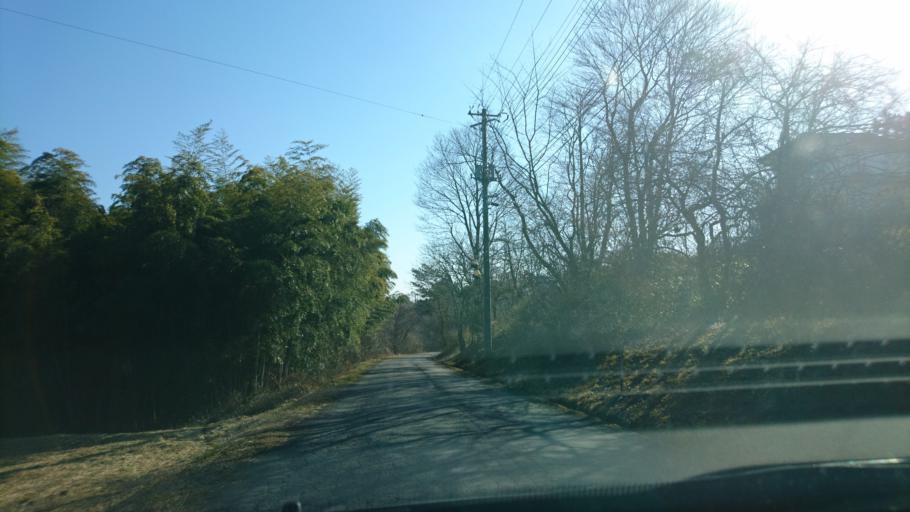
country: JP
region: Iwate
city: Ichinoseki
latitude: 38.8110
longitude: 141.2666
